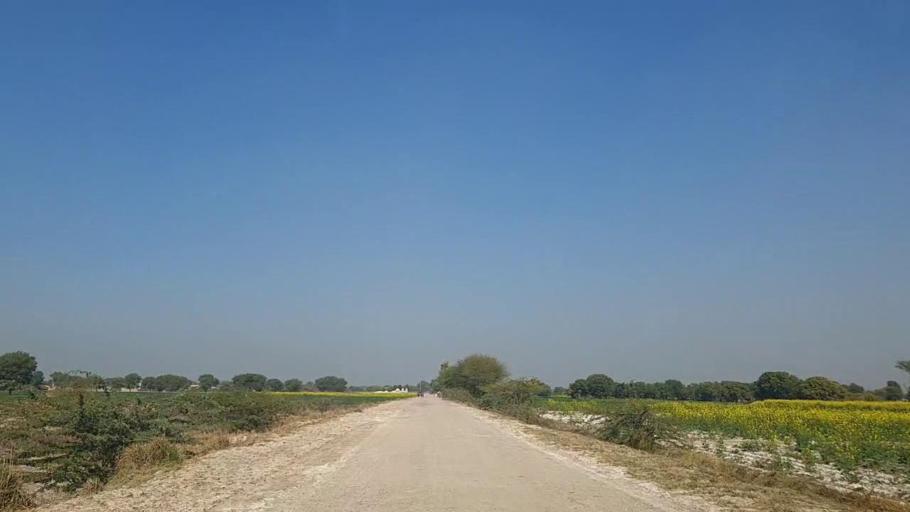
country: PK
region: Sindh
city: Nawabshah
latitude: 26.2242
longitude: 68.3379
